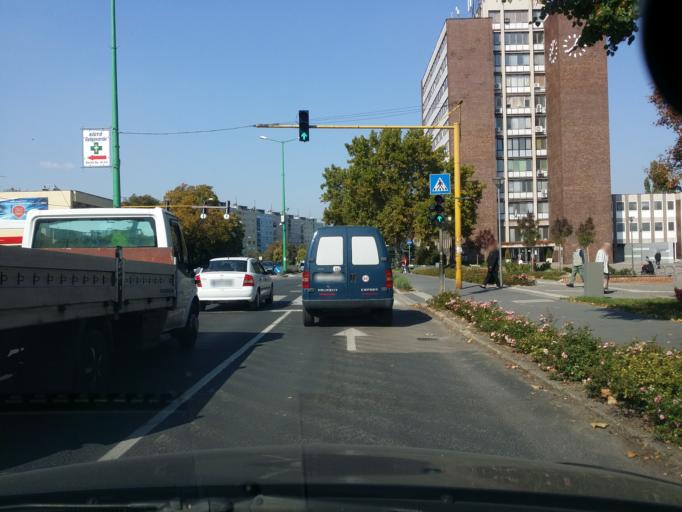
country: HU
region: Fejer
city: Dunaujvaros
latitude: 46.9644
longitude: 18.9405
